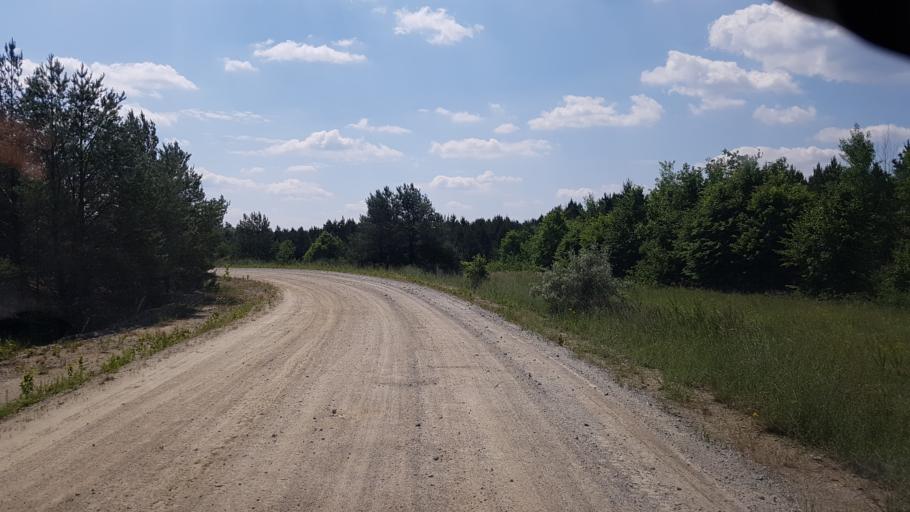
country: DE
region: Brandenburg
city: Lauchhammer
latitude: 51.5577
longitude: 13.7792
